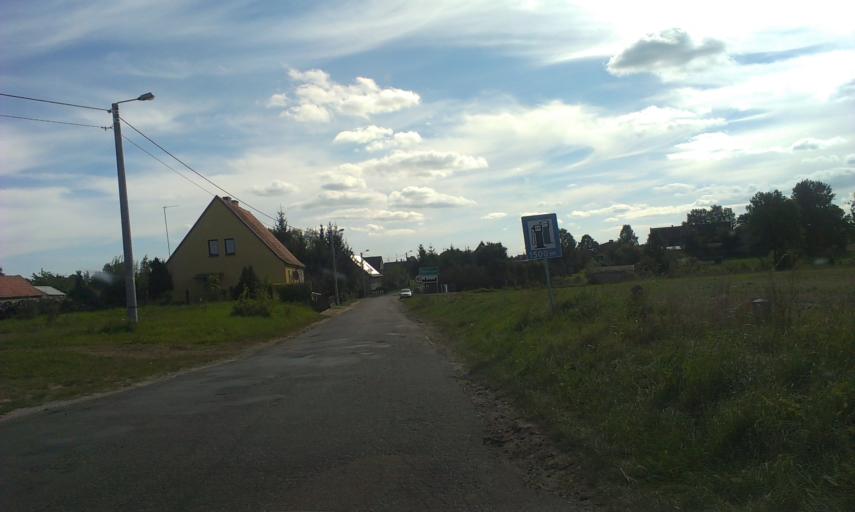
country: PL
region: Greater Poland Voivodeship
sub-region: Powiat zlotowski
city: Zlotow
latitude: 53.3092
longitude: 17.1260
